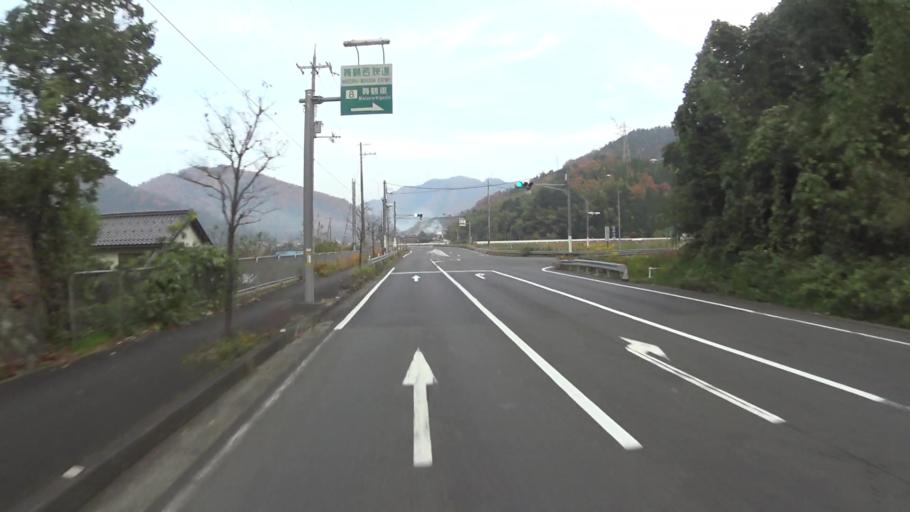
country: JP
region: Kyoto
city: Maizuru
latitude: 35.4627
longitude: 135.4190
